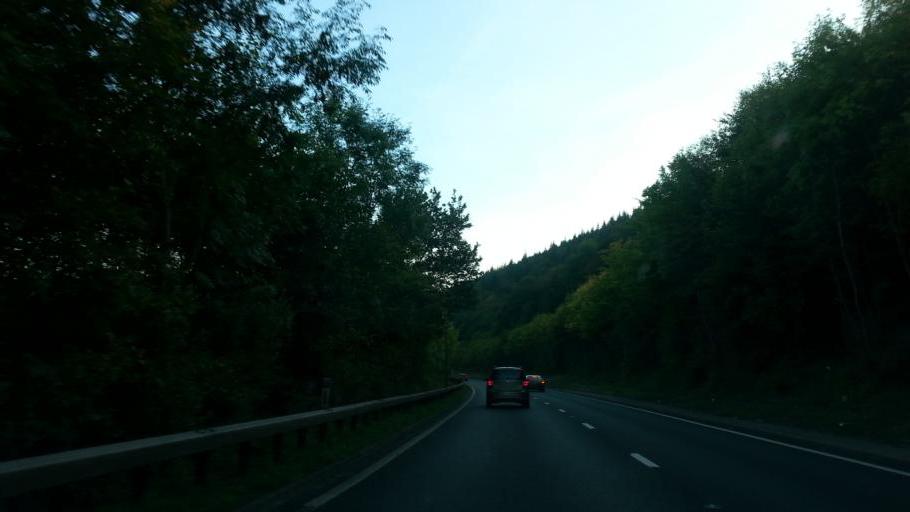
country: GB
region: Wales
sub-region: Monmouthshire
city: Monmouth
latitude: 51.8359
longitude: -2.6878
